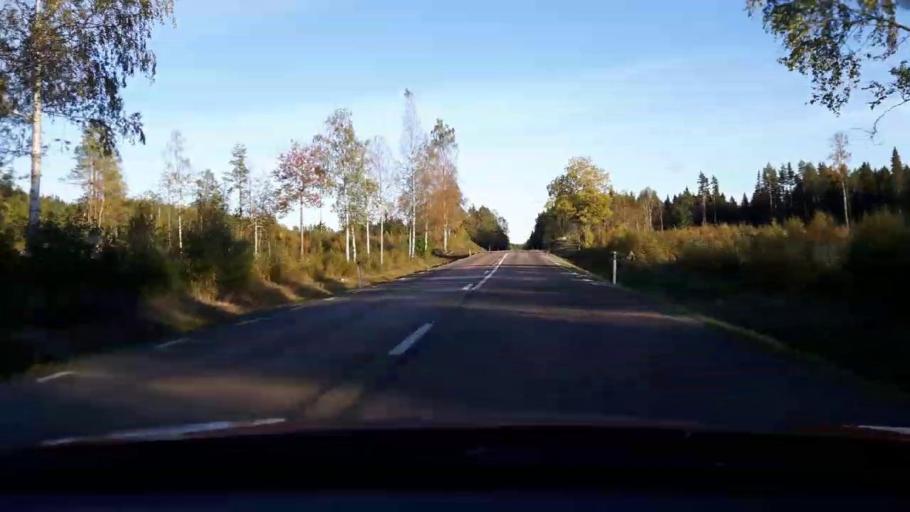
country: SE
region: Jaemtland
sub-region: OEstersunds Kommun
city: Brunflo
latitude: 63.0388
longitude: 14.8834
